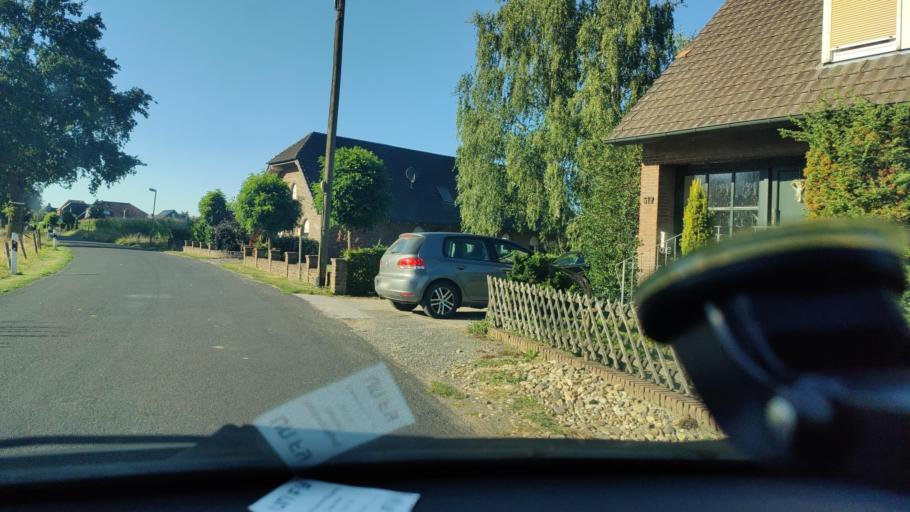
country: DE
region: North Rhine-Westphalia
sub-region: Regierungsbezirk Dusseldorf
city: Goch
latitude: 51.6753
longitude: 6.0776
